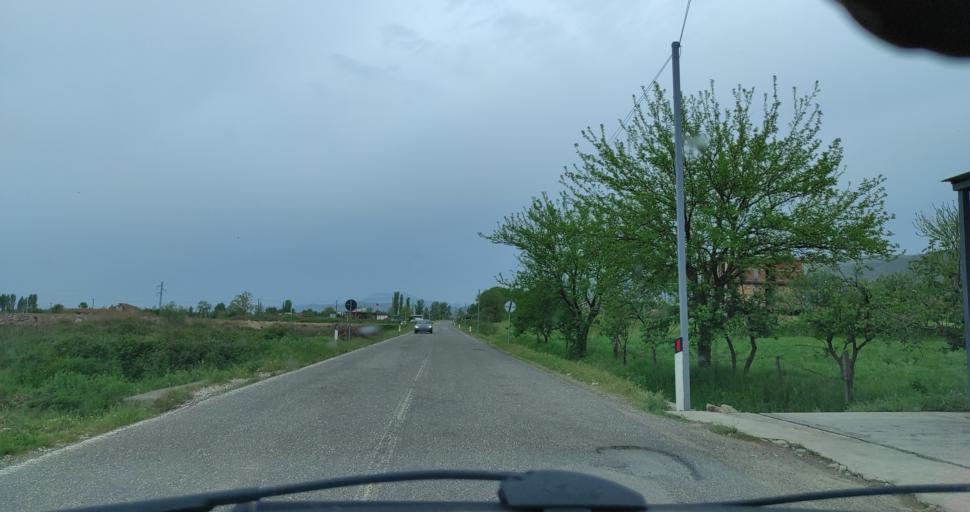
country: AL
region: Lezhe
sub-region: Rrethi i Kurbinit
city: Mamurras
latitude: 41.5963
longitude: 19.6989
